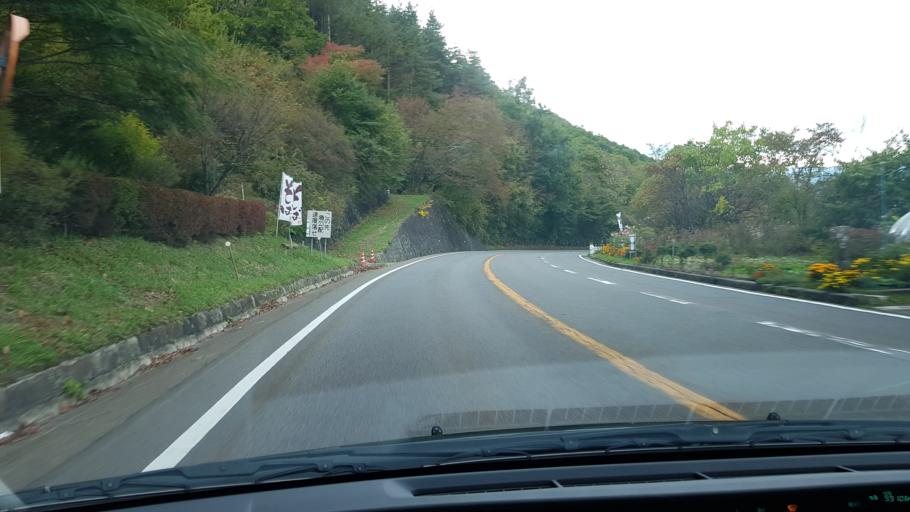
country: JP
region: Gunma
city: Nakanojomachi
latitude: 36.5933
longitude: 138.5870
